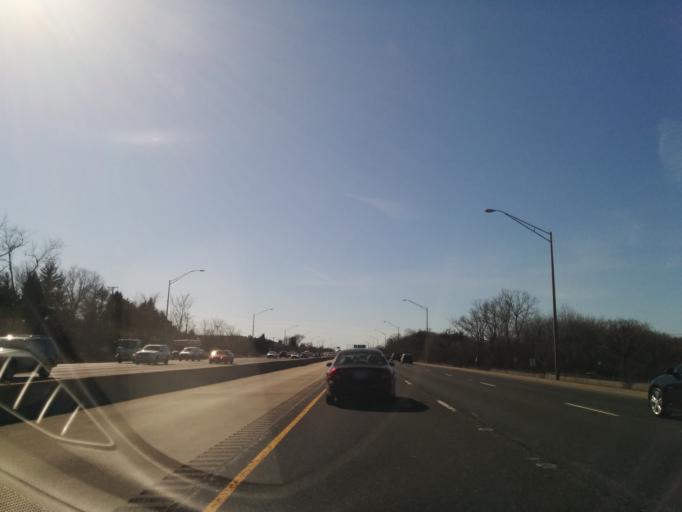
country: US
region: Illinois
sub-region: DuPage County
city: Darien
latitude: 41.7247
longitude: -87.9917
